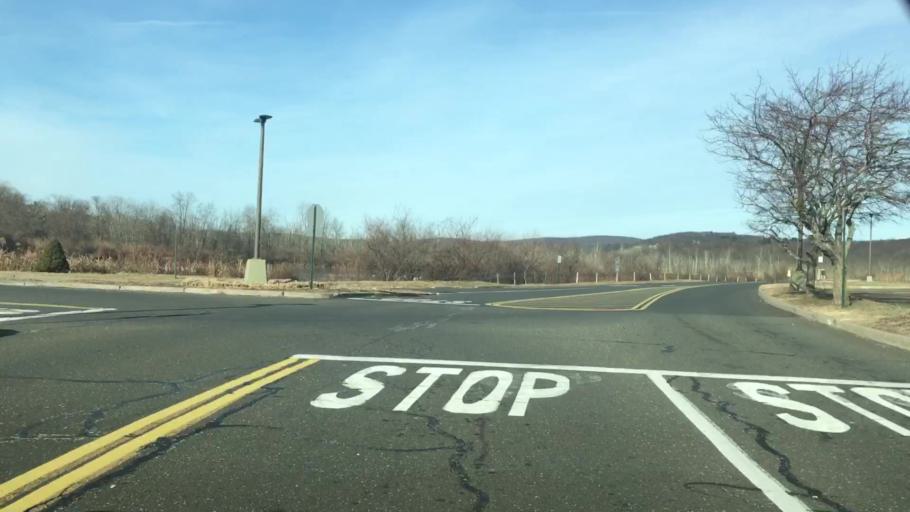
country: US
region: Connecticut
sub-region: Fairfield County
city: Danbury
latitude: 41.3775
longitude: -73.4842
